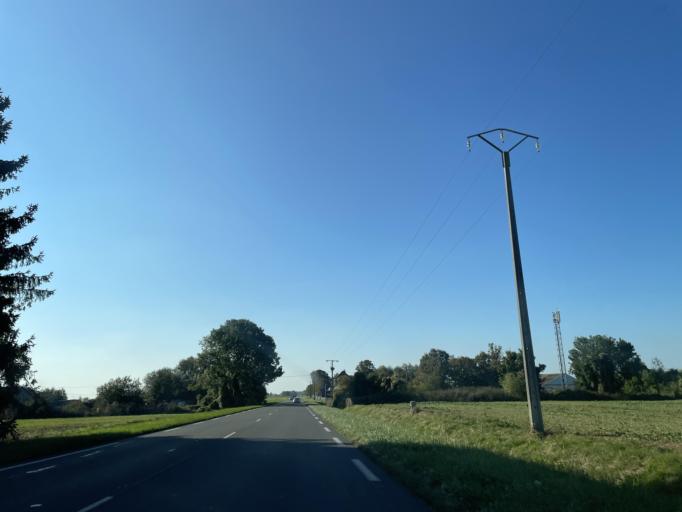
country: FR
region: Ile-de-France
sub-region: Departement de Seine-et-Marne
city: Pommeuse
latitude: 48.8313
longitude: 3.0133
